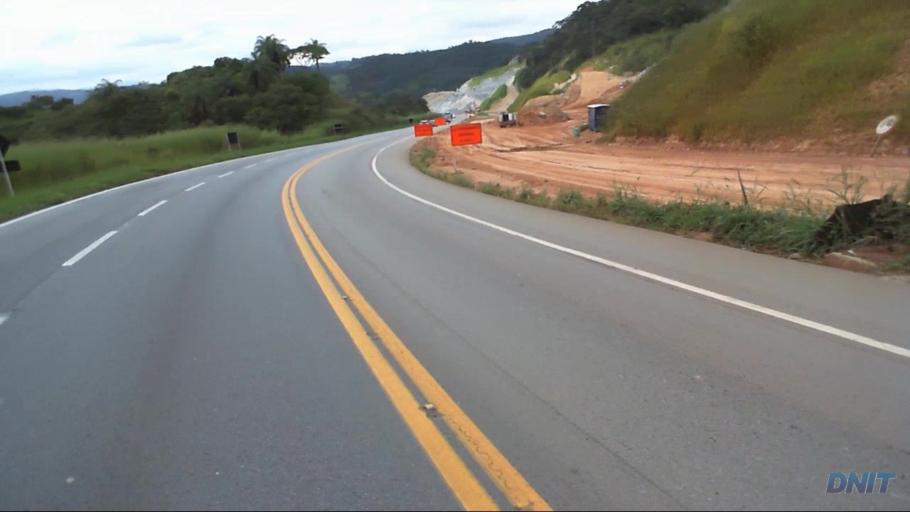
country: BR
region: Minas Gerais
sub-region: Caete
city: Caete
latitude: -19.7883
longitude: -43.6720
